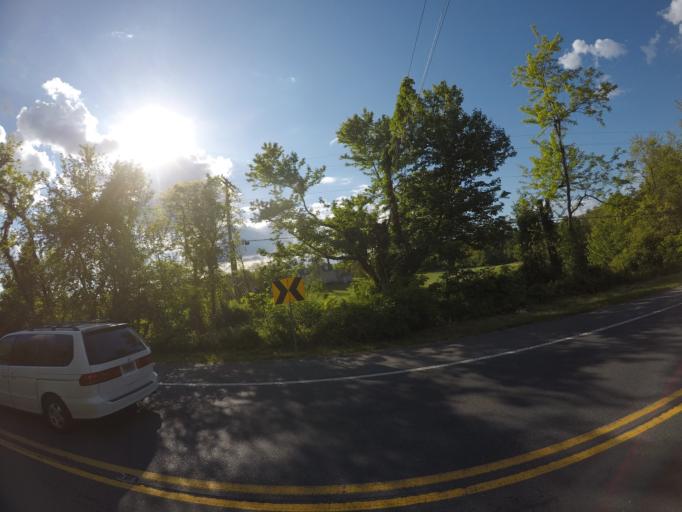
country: US
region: Maryland
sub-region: Montgomery County
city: Damascus
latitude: 39.3226
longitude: -77.1948
